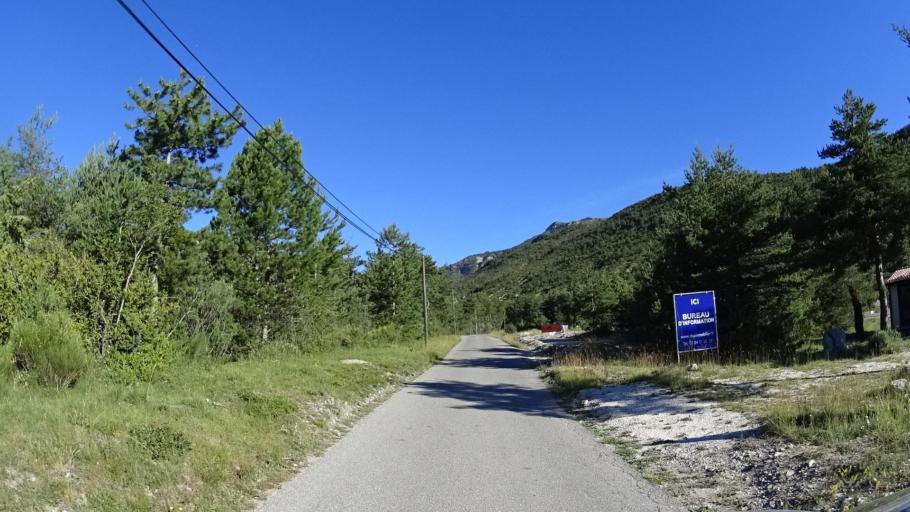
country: FR
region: Provence-Alpes-Cote d'Azur
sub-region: Departement des Alpes-de-Haute-Provence
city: Castellane
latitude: 43.8778
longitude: 6.5043
